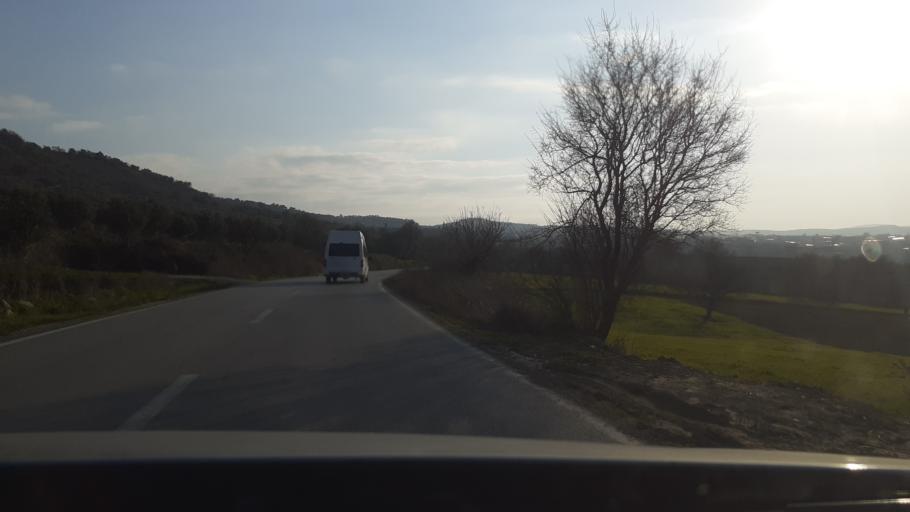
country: TR
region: Hatay
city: Oymakli
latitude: 36.1193
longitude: 36.3050
